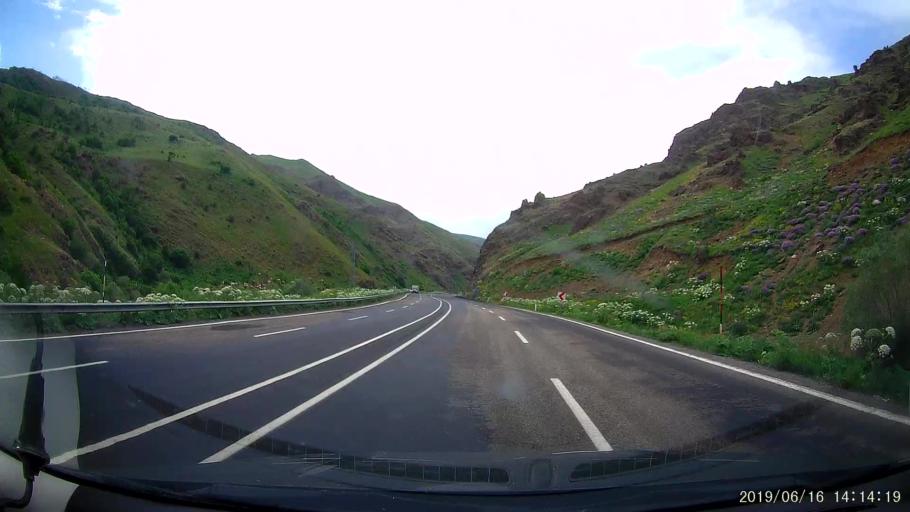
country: TR
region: Agri
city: Tahir
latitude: 39.7953
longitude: 42.4998
